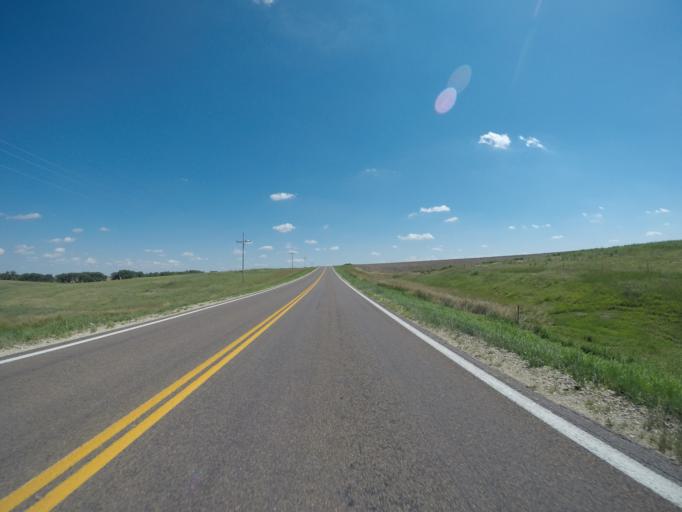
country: US
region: Kansas
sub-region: Sheridan County
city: Hoxie
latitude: 39.1700
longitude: -100.4428
